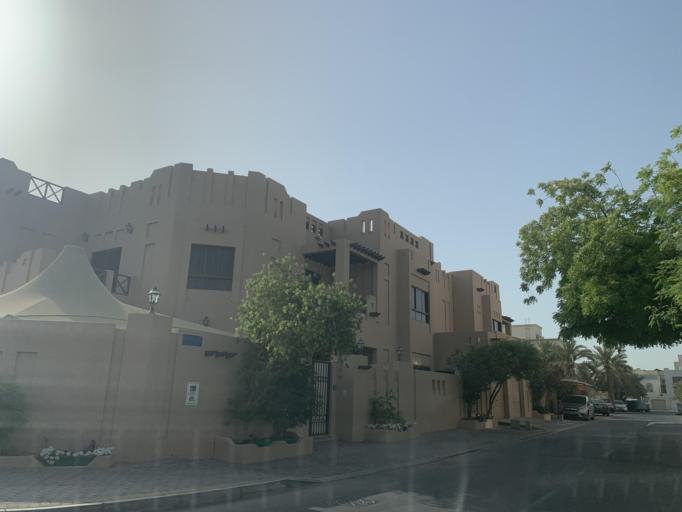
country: BH
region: Northern
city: Ar Rifa'
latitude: 26.1439
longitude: 50.5841
